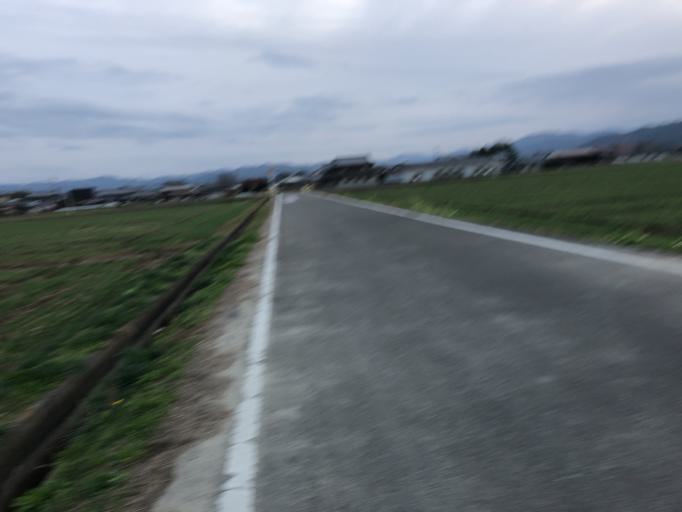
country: JP
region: Kyoto
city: Kameoka
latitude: 35.0602
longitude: 135.5618
